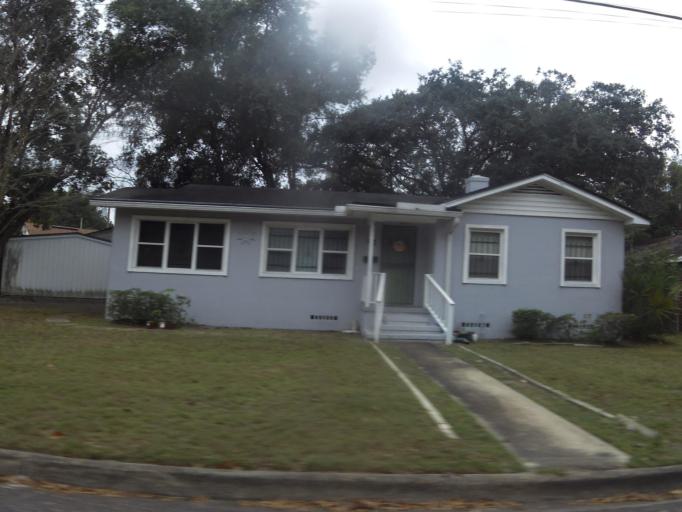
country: US
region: Florida
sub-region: Duval County
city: Jacksonville
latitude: 30.3796
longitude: -81.6515
